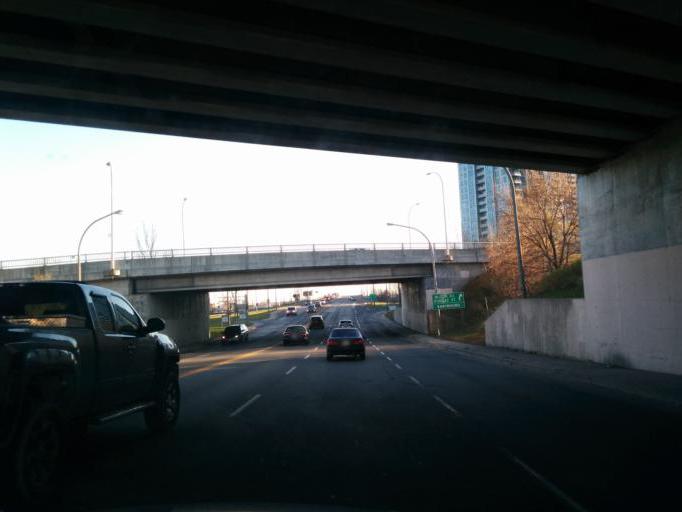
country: CA
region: Ontario
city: Etobicoke
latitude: 43.6416
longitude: -79.5353
